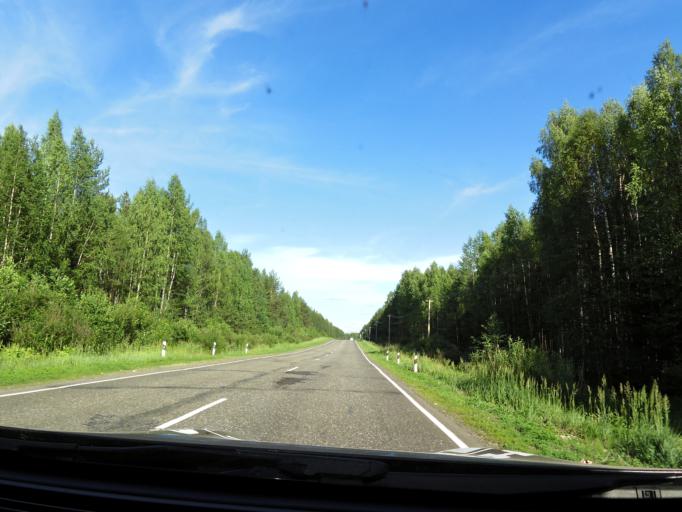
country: RU
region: Kirov
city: Belaya Kholunitsa
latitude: 58.9154
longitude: 51.1514
